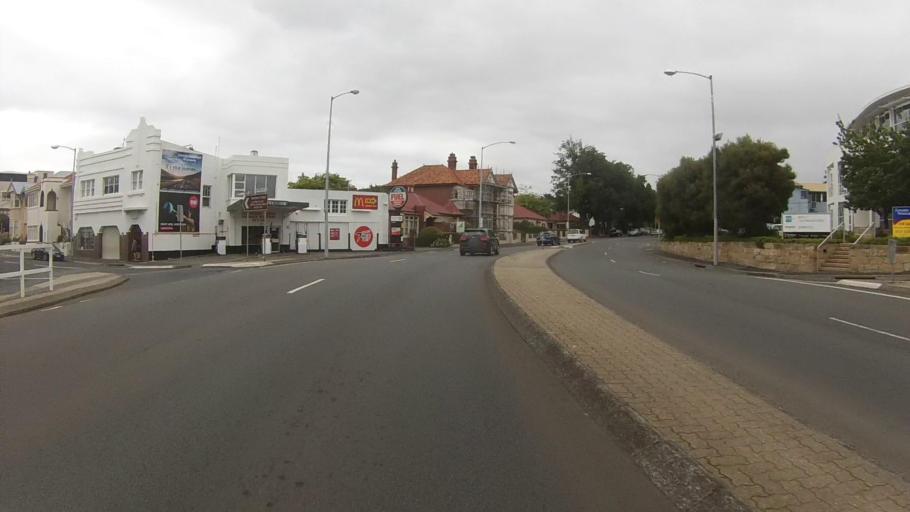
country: AU
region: Tasmania
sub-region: Hobart
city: Sandy Bay
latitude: -42.8891
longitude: 147.3303
